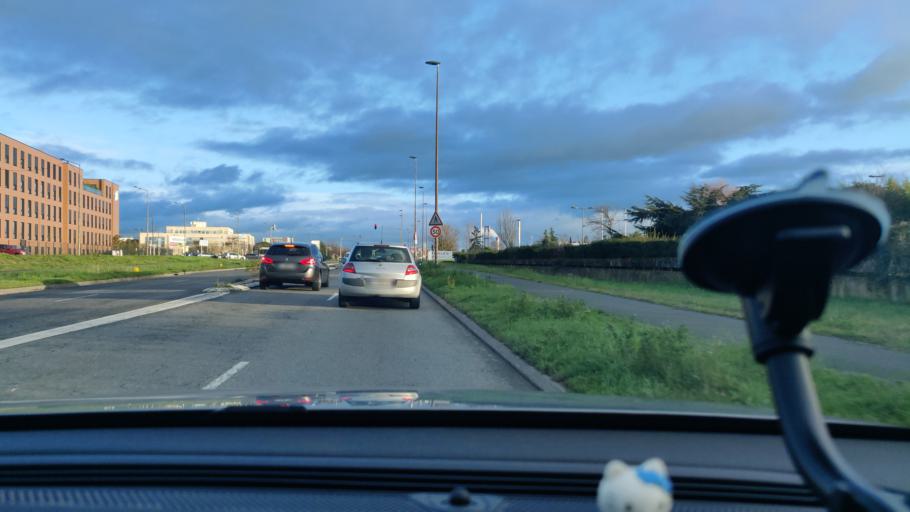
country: FR
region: Midi-Pyrenees
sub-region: Departement de la Haute-Garonne
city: Cugnaux
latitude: 43.5654
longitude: 1.3821
